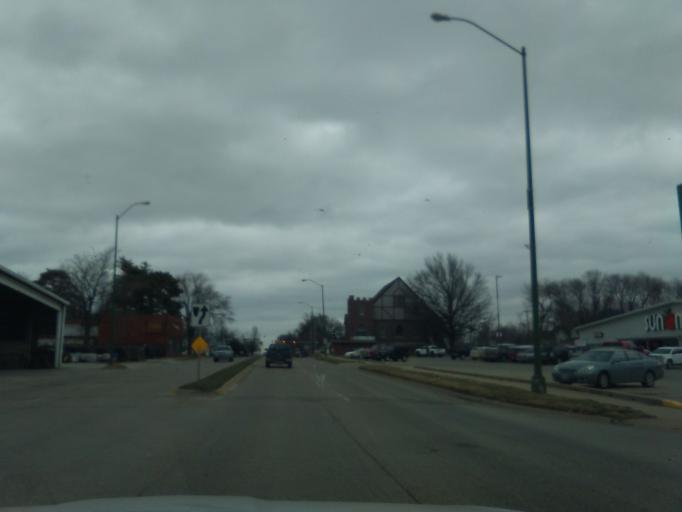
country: US
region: Nebraska
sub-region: Richardson County
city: Falls City
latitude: 40.0636
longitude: -95.6018
